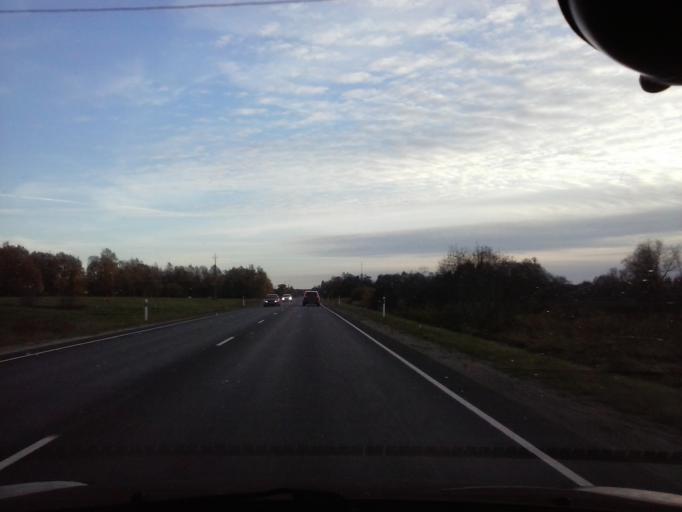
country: EE
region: Harju
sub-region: Nissi vald
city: Turba
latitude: 58.9168
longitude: 24.1123
